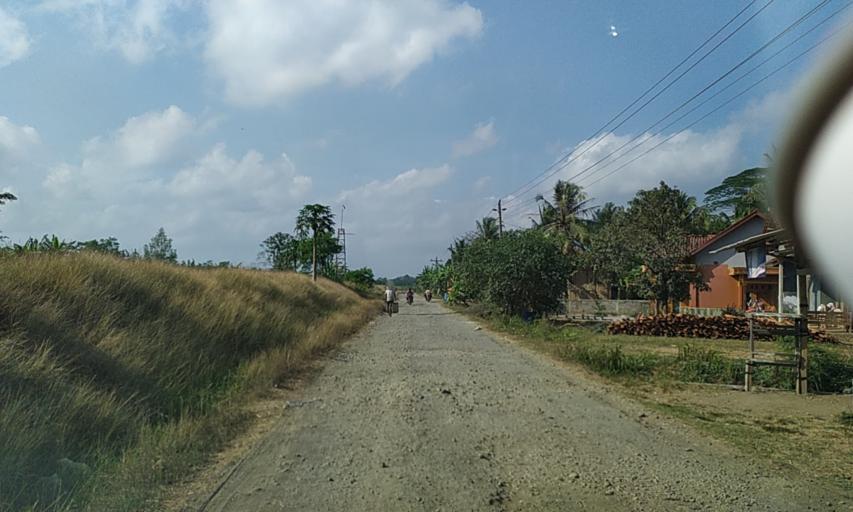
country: ID
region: Central Java
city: Sidakaya
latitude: -7.5951
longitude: 108.8713
